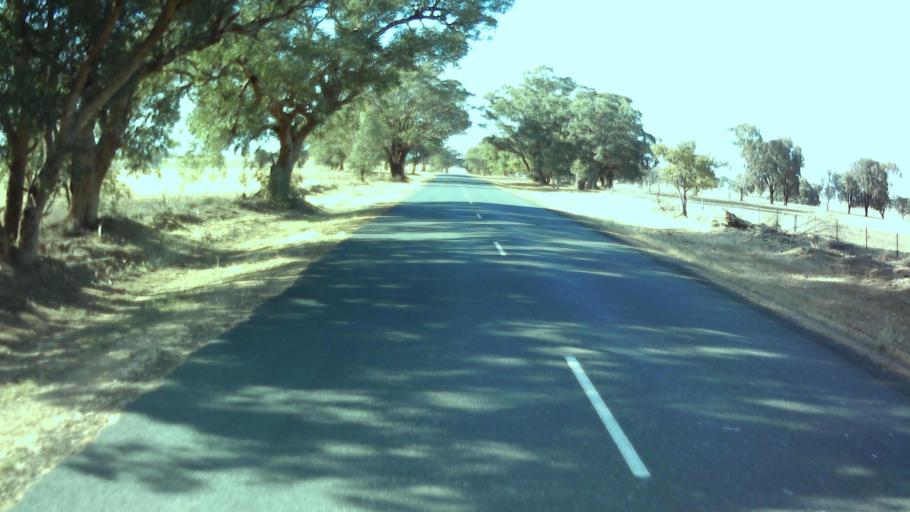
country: AU
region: New South Wales
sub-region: Weddin
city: Grenfell
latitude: -33.9613
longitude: 148.1401
